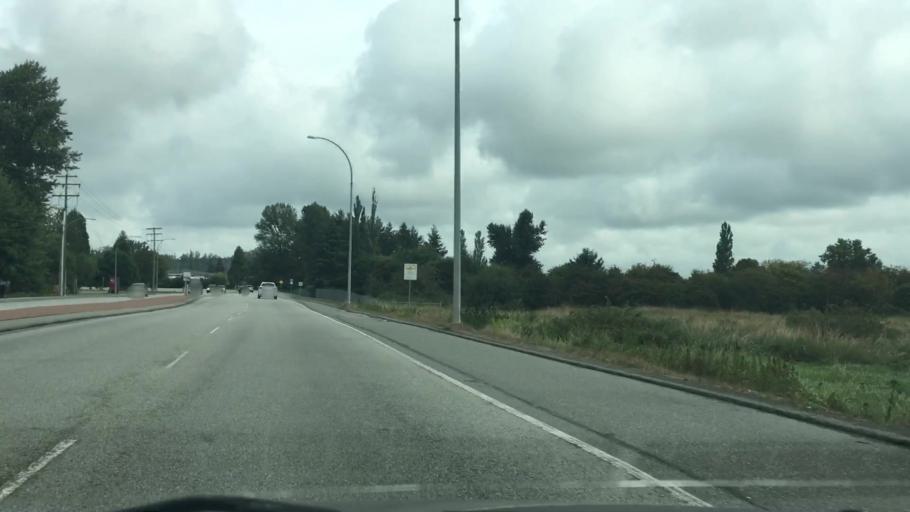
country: CA
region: British Columbia
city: Langley
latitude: 49.1068
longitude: -122.6427
